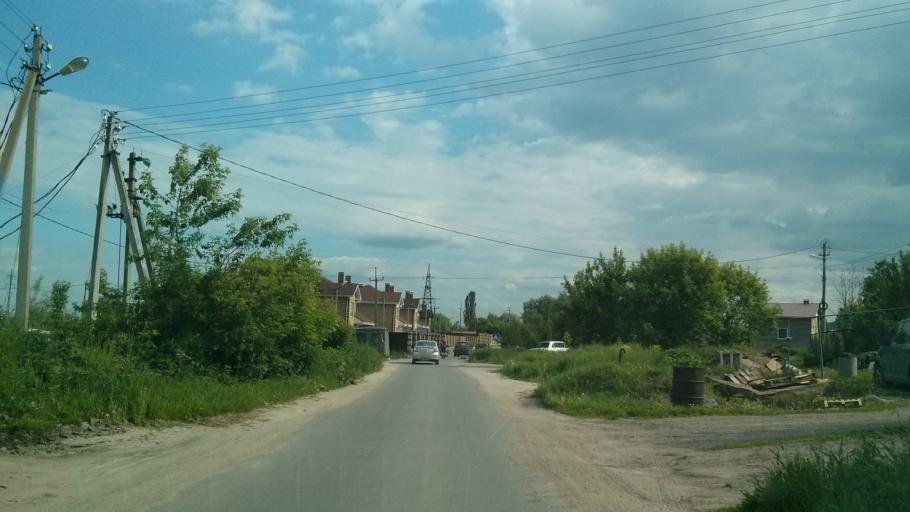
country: RU
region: Nizjnij Novgorod
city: Afonino
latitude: 56.2833
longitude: 44.1013
